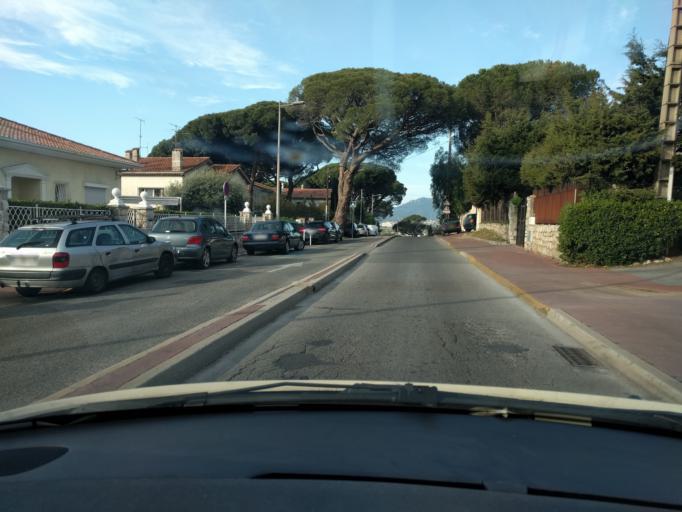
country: FR
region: Provence-Alpes-Cote d'Azur
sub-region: Departement des Alpes-Maritimes
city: Cannes
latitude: 43.5608
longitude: 6.9740
